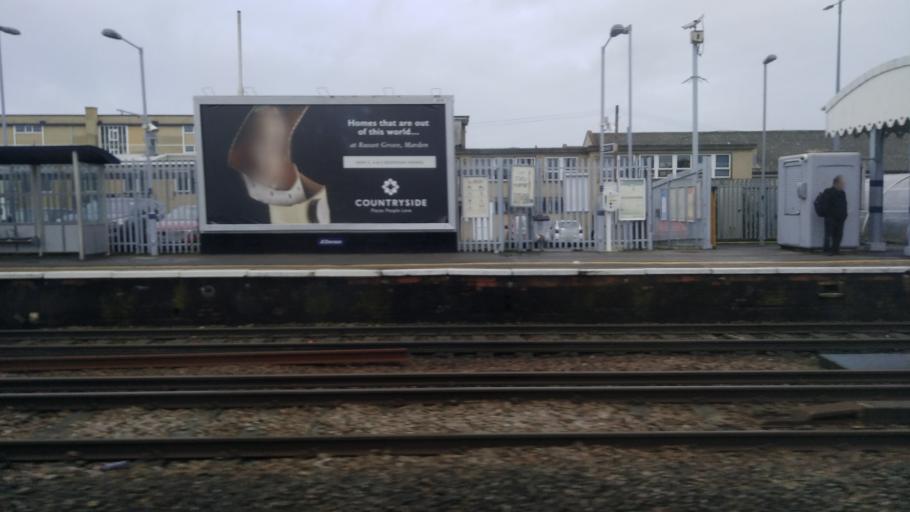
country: GB
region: England
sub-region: Kent
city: Paddock Wood
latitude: 51.1824
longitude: 0.3893
